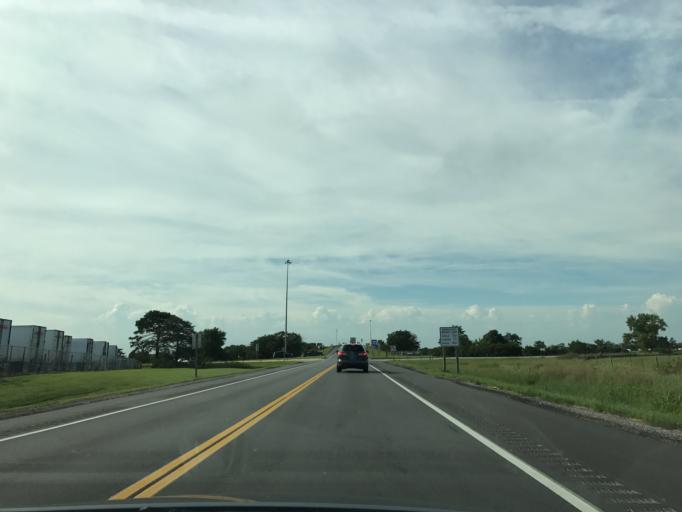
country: US
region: Nebraska
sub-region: Seward County
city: Milford
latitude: 40.8253
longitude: -97.1019
